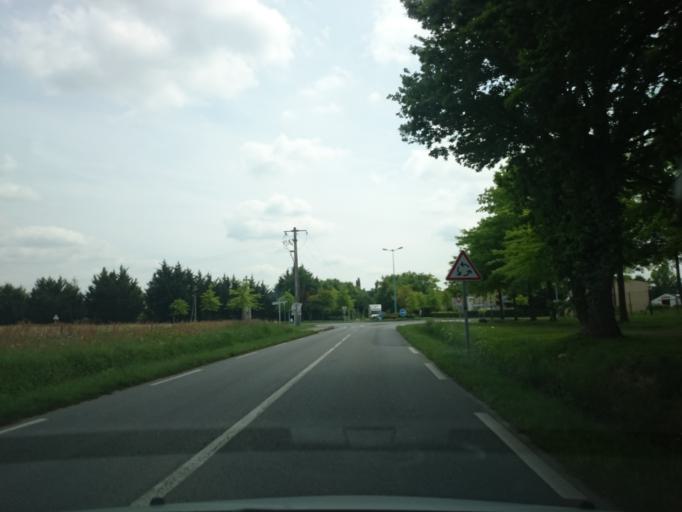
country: FR
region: Pays de la Loire
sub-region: Departement de la Loire-Atlantique
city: Pont-Saint-Martin
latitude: 47.1170
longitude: -1.5804
